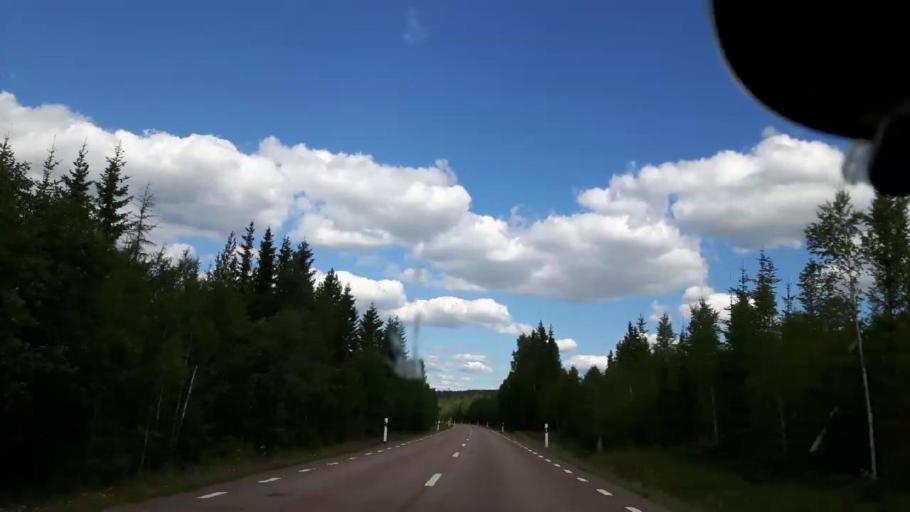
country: SE
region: Jaemtland
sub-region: Ragunda Kommun
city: Hammarstrand
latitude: 62.8982
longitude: 16.6967
